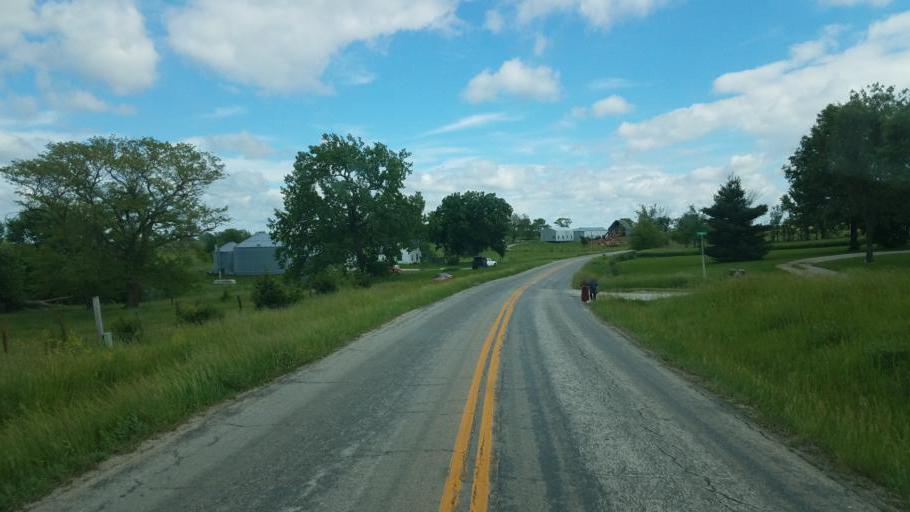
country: US
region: Missouri
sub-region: Mercer County
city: Princeton
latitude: 40.2789
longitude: -93.6766
